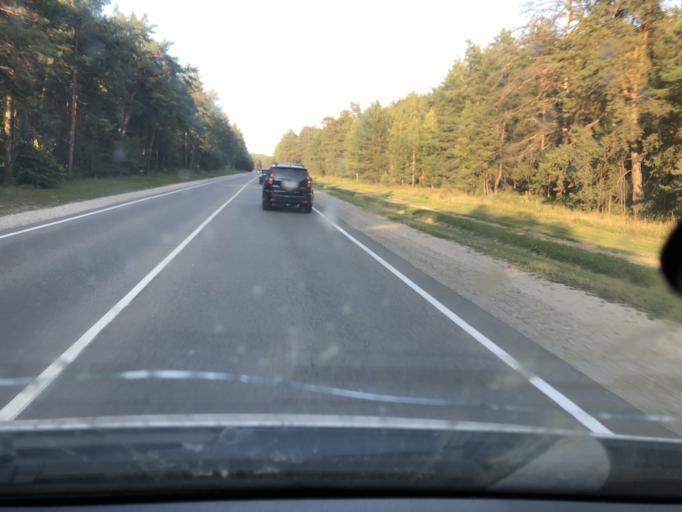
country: RU
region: Kaluga
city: Peremyshl'
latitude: 54.3510
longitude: 36.1945
